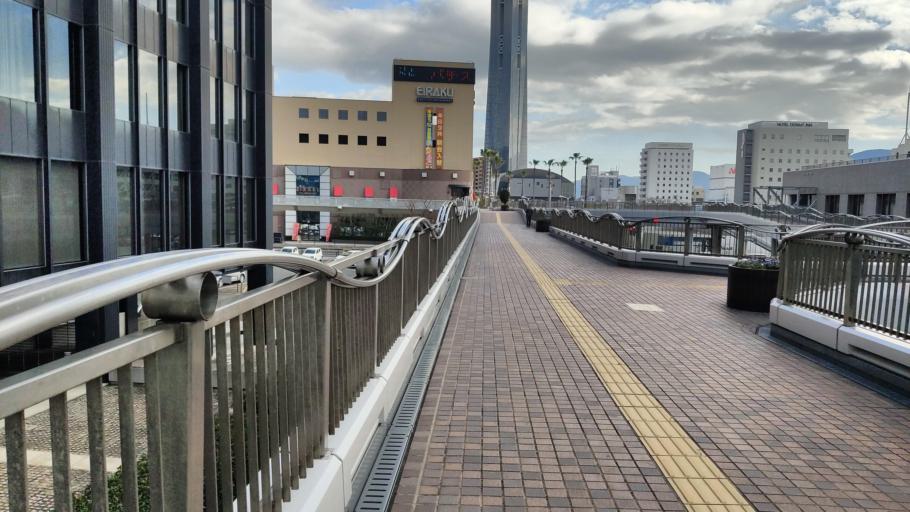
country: JP
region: Yamaguchi
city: Shimonoseki
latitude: 33.9501
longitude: 130.9250
